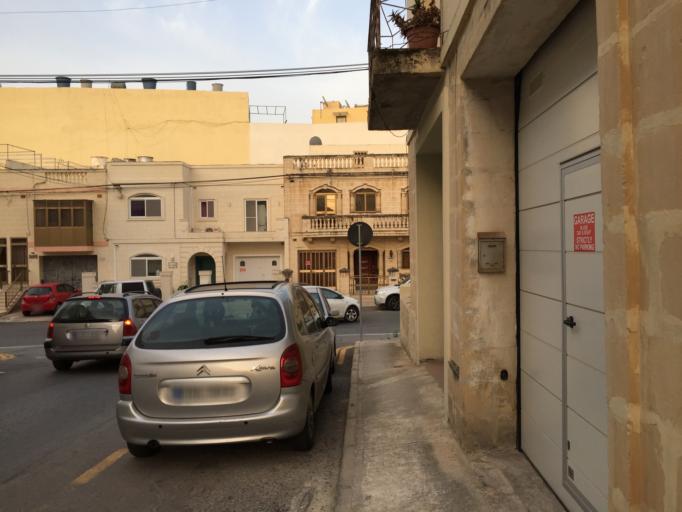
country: MT
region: Il-Fgura
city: Fgura
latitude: 35.8742
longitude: 14.5215
